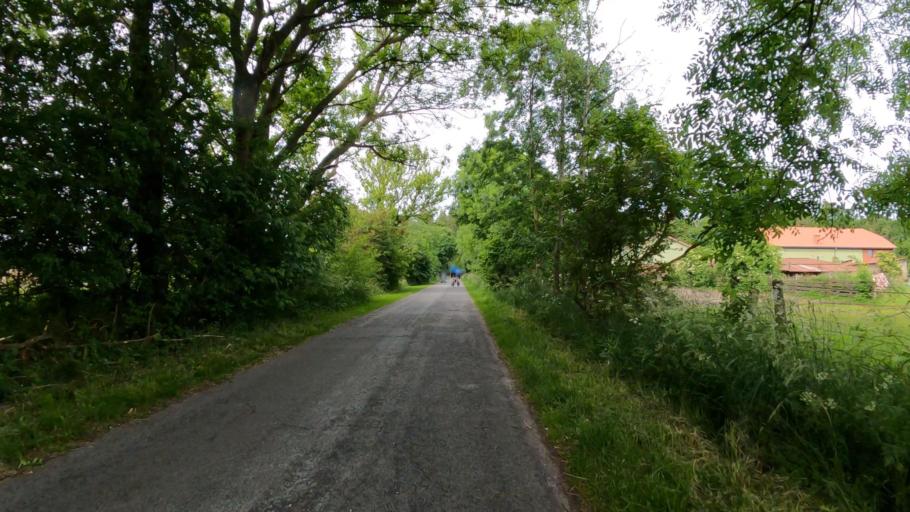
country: DE
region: Schleswig-Holstein
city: Hartenholm
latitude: 53.8918
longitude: 10.0831
